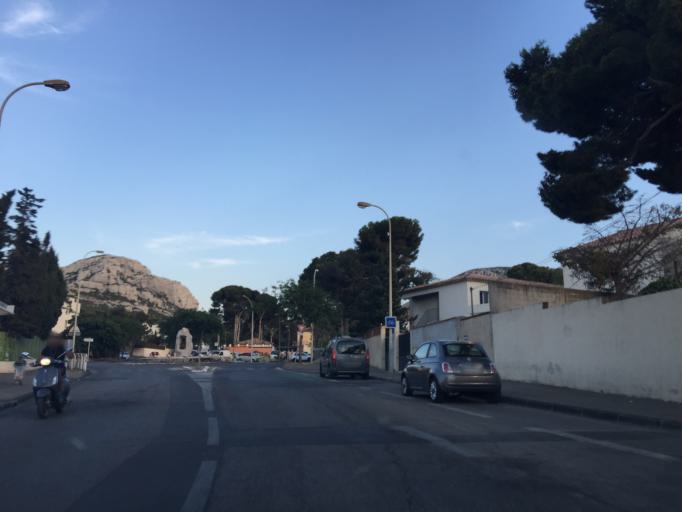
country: FR
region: Provence-Alpes-Cote d'Azur
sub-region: Departement des Bouches-du-Rhone
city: Marseille 09
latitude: 43.2297
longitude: 5.4013
